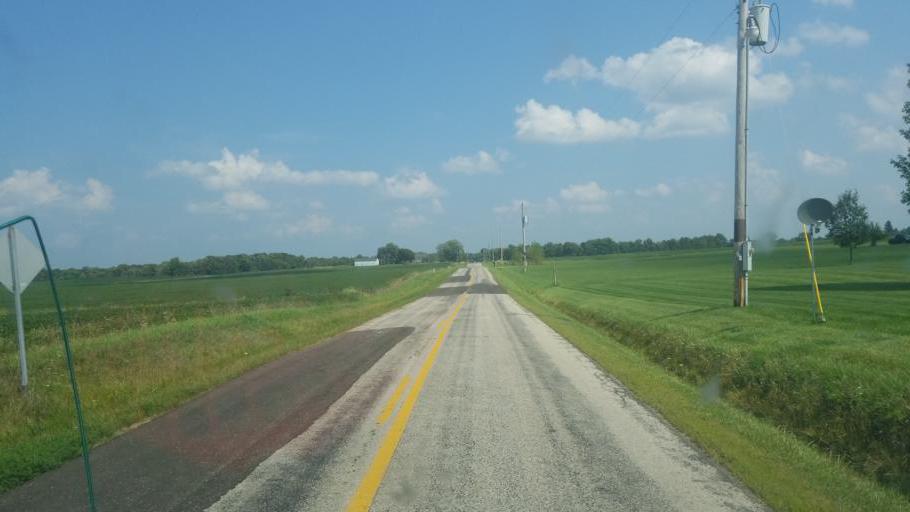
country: US
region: Ohio
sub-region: Huron County
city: New London
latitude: 41.0657
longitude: -82.3454
